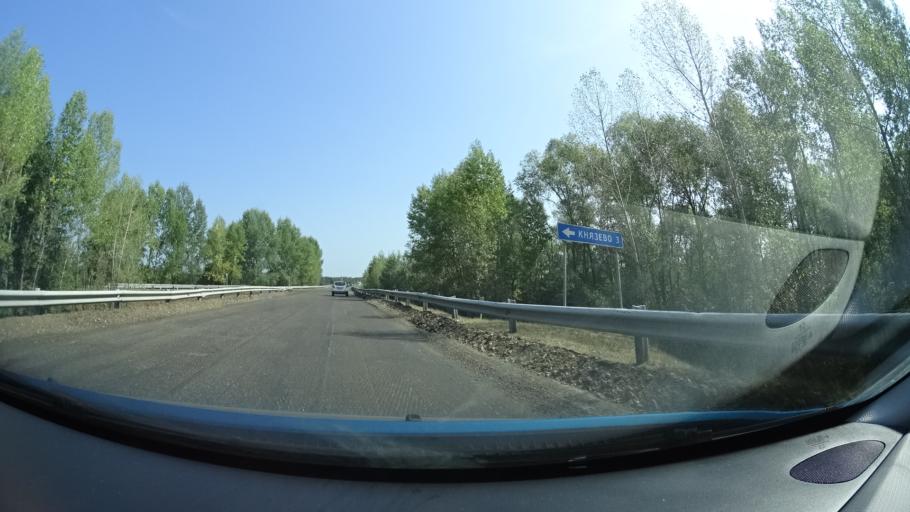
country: RU
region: Bashkortostan
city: Ulukulevo
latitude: 54.4531
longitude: 56.4772
